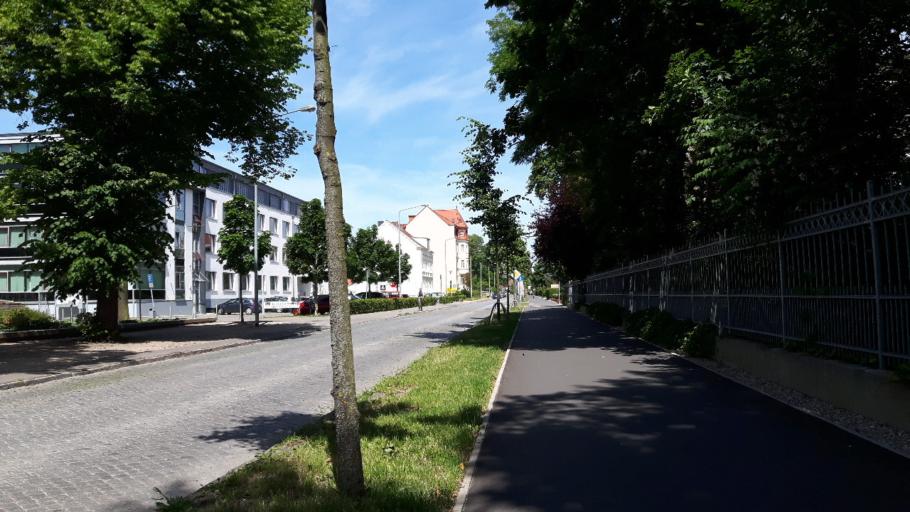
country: DE
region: Saxony-Anhalt
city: Wittenburg
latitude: 51.8720
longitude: 12.6403
